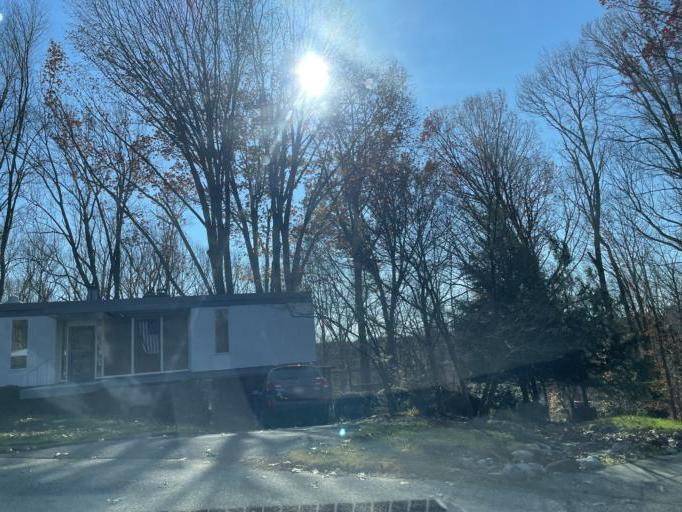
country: US
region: Maryland
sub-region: Baltimore County
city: Mays Chapel
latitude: 39.3934
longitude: -76.6592
